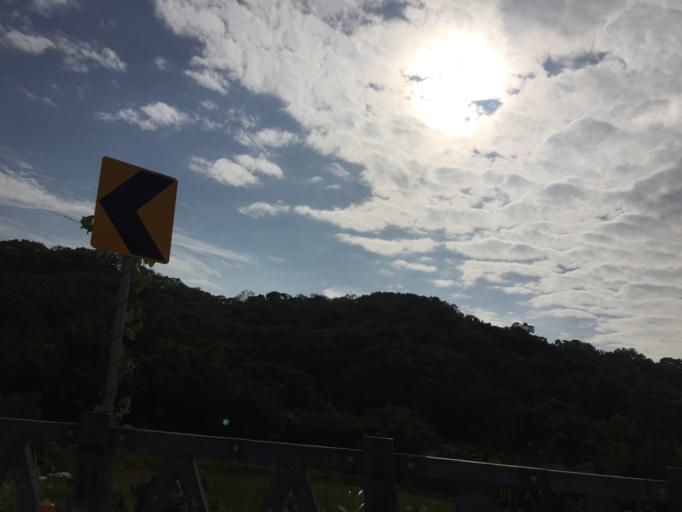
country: TW
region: Taiwan
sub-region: Hsinchu
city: Hsinchu
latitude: 24.7740
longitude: 120.9494
